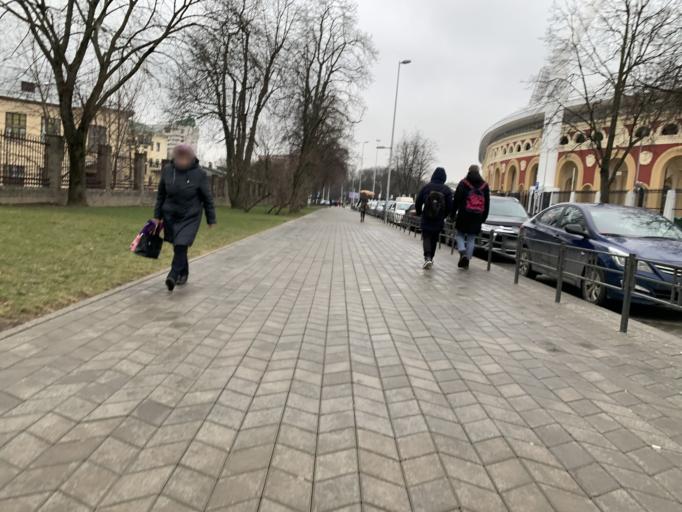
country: BY
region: Minsk
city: Minsk
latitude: 53.8965
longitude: 27.5621
